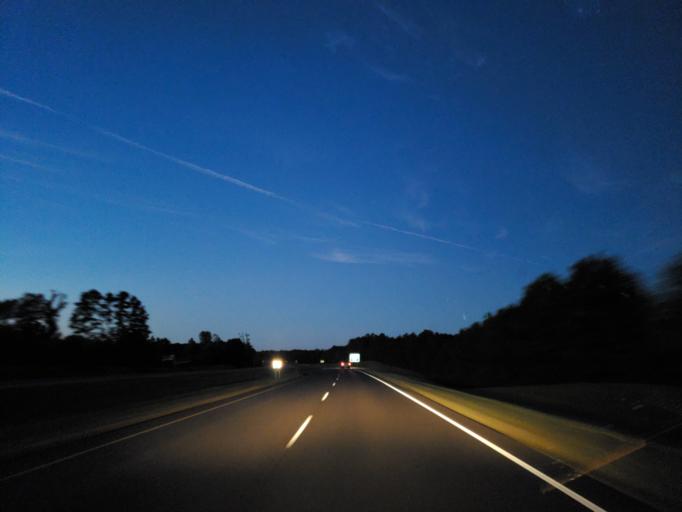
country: US
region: Mississippi
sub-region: Clarke County
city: Quitman
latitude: 32.0428
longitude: -88.6775
